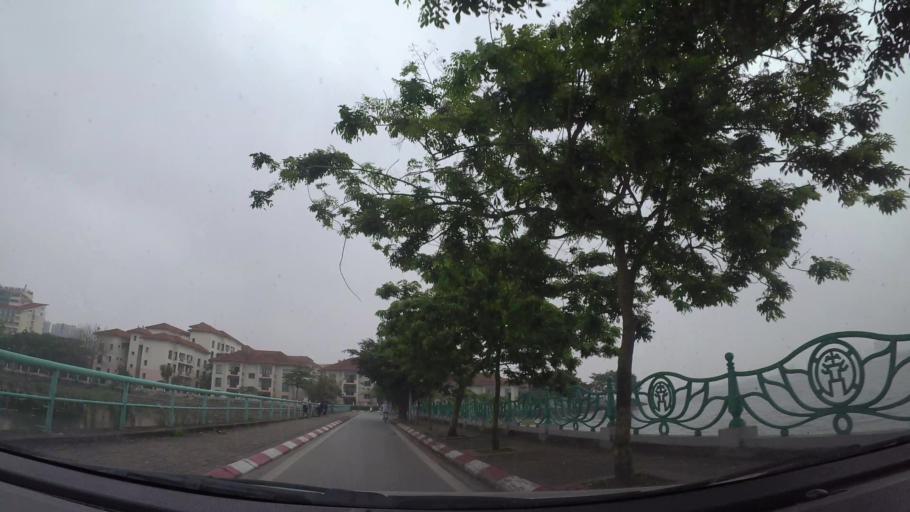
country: VN
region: Ha Noi
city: Tay Ho
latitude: 21.0681
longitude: 105.8190
